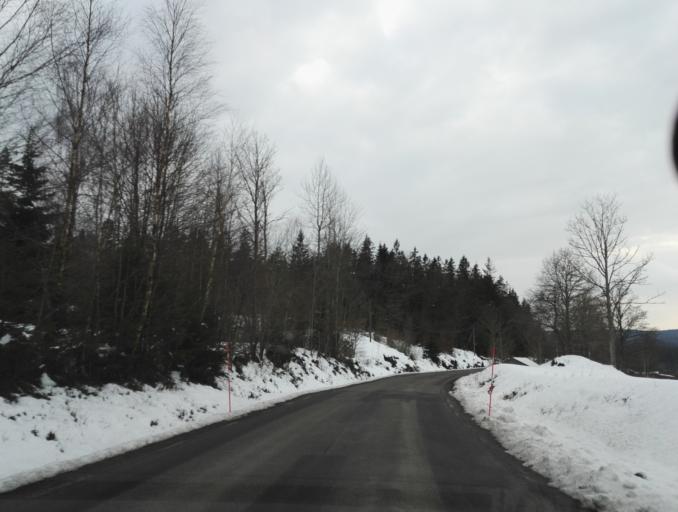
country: SE
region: Vaestra Goetaland
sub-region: Alingsas Kommun
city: Ingared
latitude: 57.8073
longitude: 12.5384
